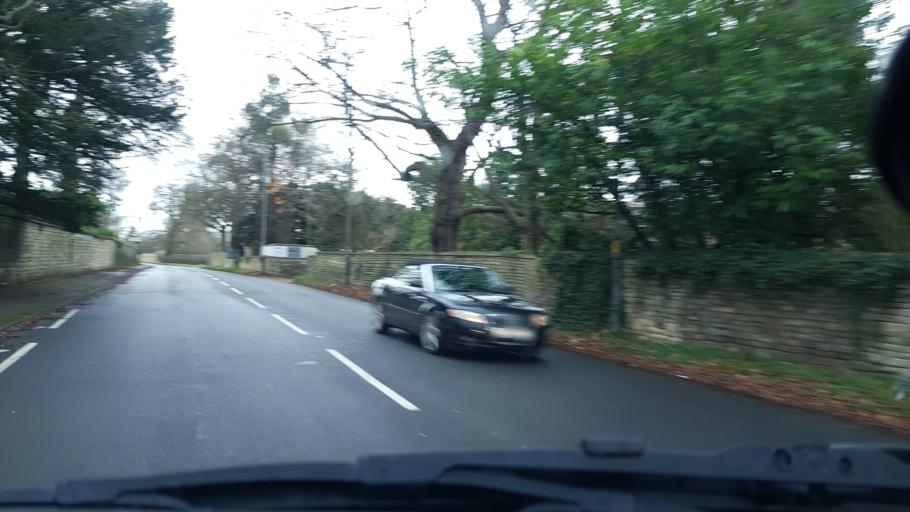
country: GB
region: England
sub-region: Gloucestershire
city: Charlton Kings
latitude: 51.9132
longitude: -2.0404
